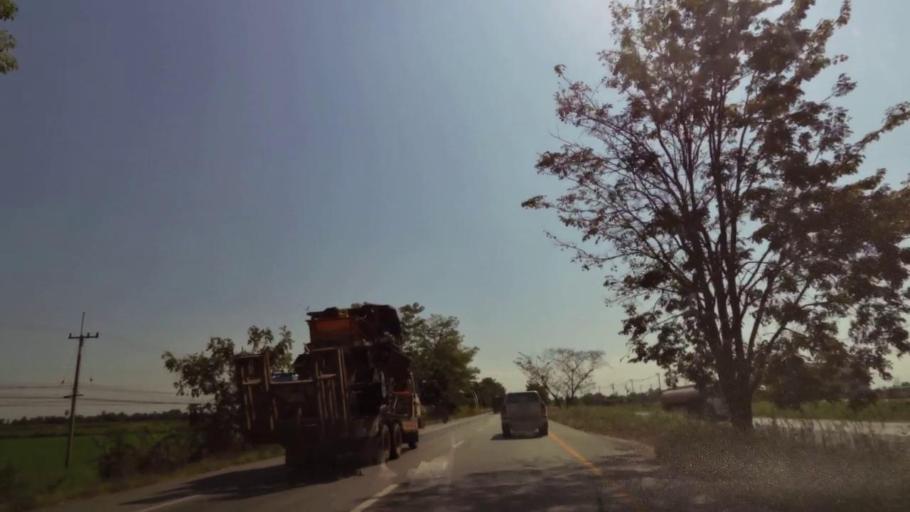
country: TH
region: Nakhon Sawan
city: Kao Liao
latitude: 15.8322
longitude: 100.1182
